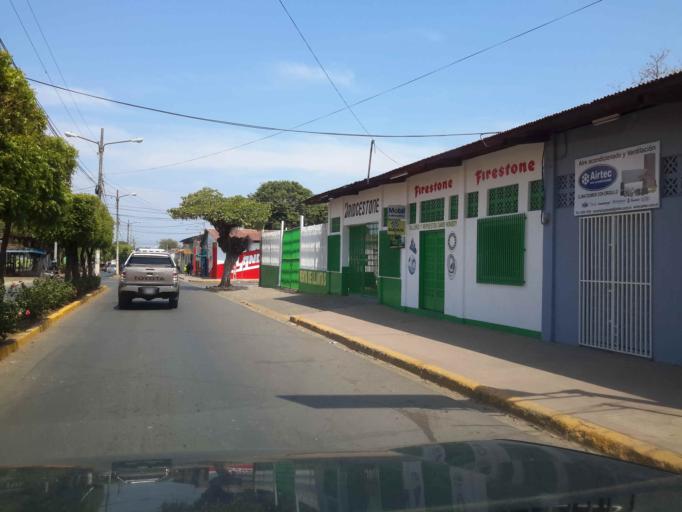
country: NI
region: Granada
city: Granada
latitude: 11.9367
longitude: -85.9578
